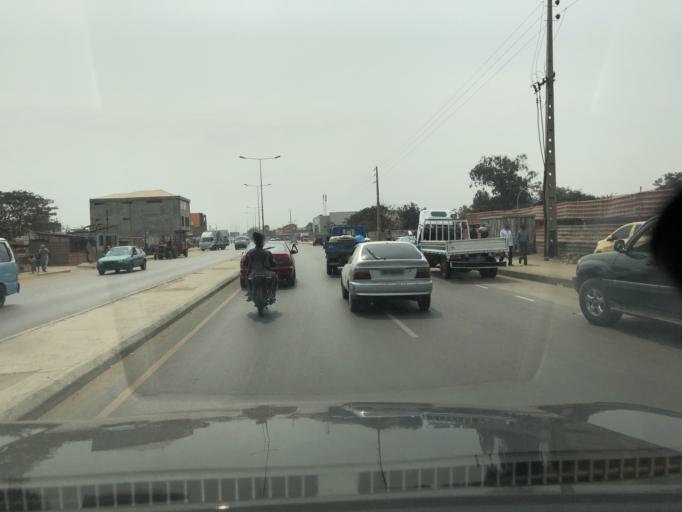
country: AO
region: Luanda
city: Luanda
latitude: -8.8007
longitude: 13.3122
